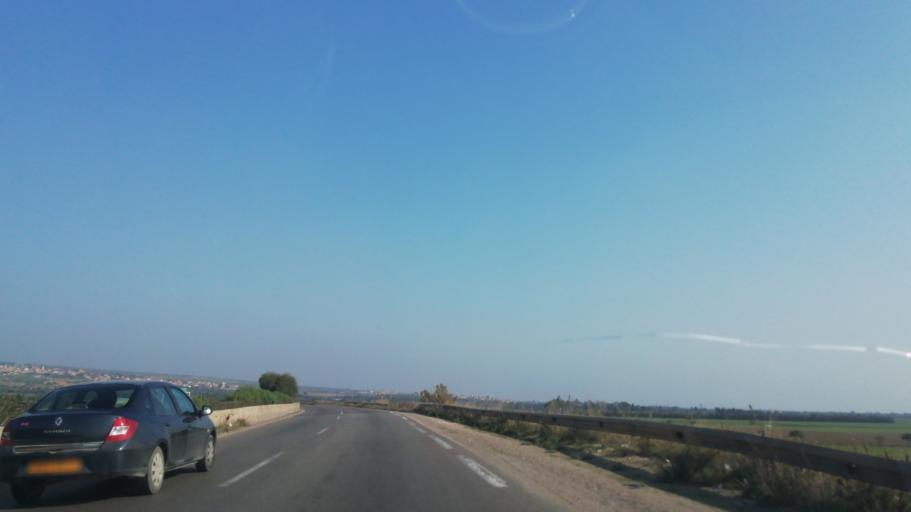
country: DZ
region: Oran
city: Bou Tlelis
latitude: 35.5682
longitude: -0.8857
